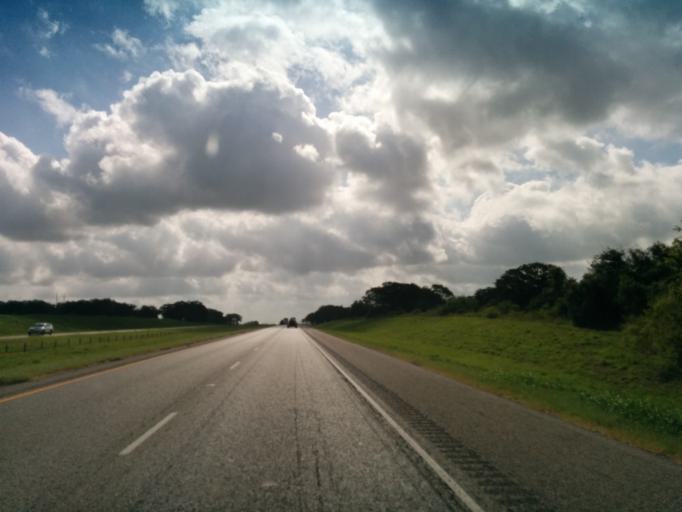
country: US
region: Texas
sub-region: Gonzales County
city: Waelder
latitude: 29.6568
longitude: -97.4283
